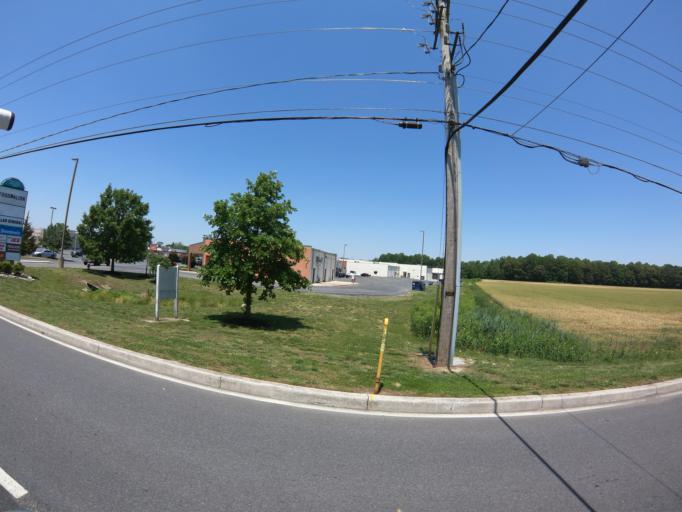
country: US
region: Delaware
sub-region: Kent County
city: Harrington
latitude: 38.9242
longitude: -75.5649
